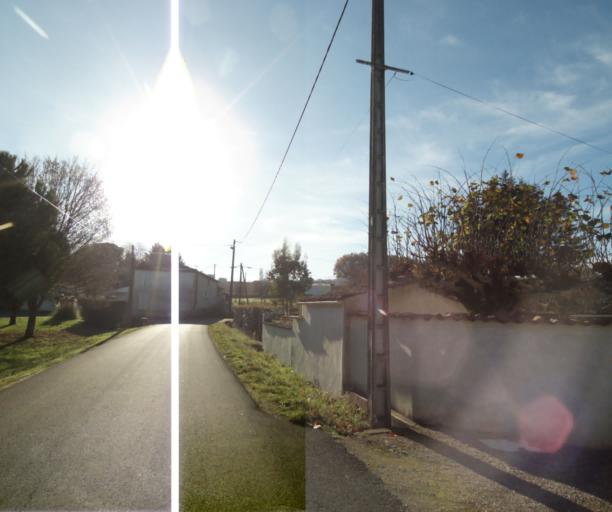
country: FR
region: Poitou-Charentes
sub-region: Departement de la Charente-Maritime
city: Burie
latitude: 45.7736
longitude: -0.4257
